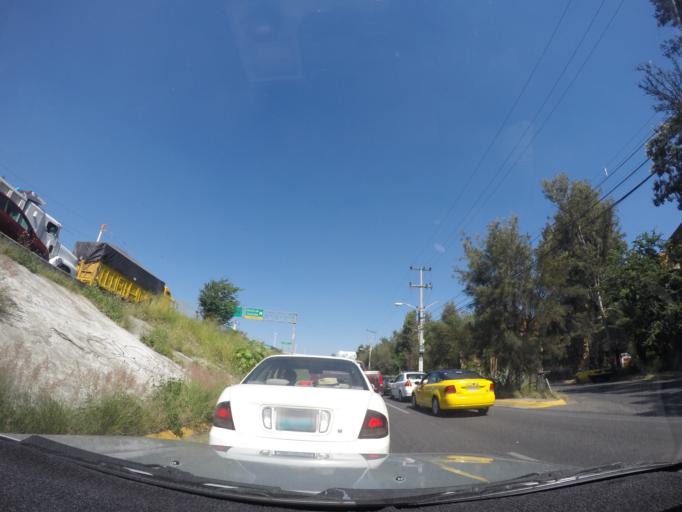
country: MX
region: Jalisco
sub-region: Tonala
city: Mismaloya (Fraccionamiento Pedregal de Santa Martha)
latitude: 20.6054
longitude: -103.1417
